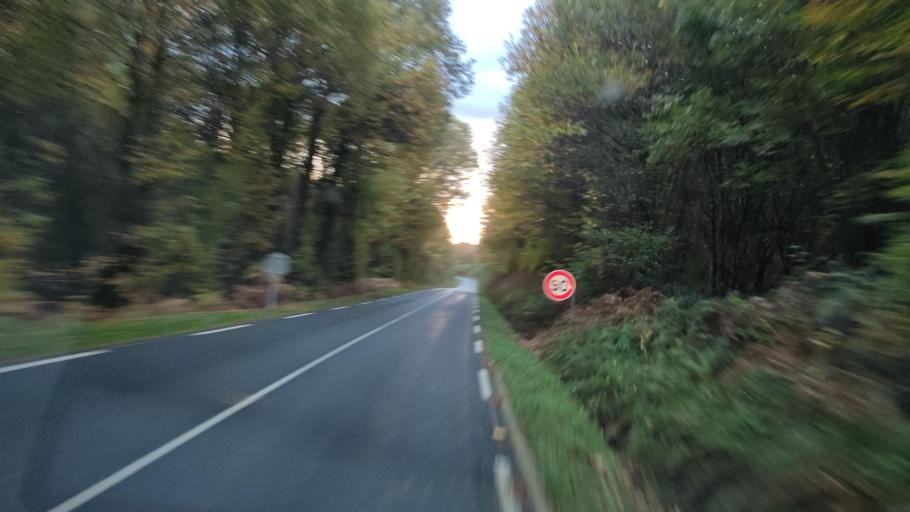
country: FR
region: Limousin
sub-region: Departement de la Haute-Vienne
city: Ambazac
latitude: 45.9961
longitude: 1.4495
